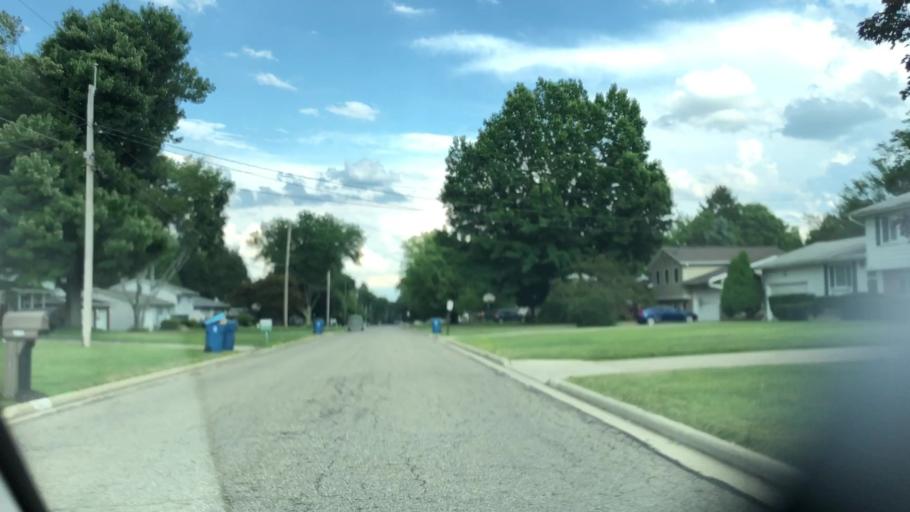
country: US
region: Ohio
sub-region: Summit County
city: Norton
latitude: 41.0367
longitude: -81.6337
